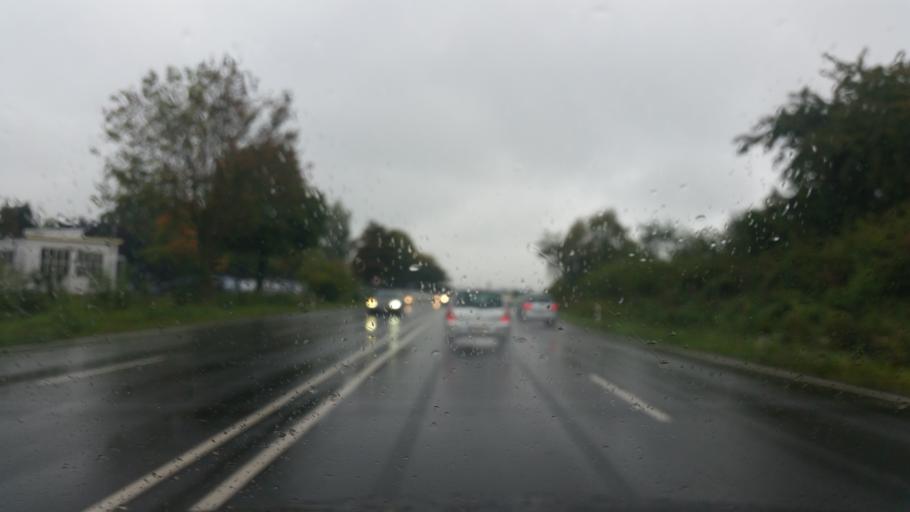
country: DE
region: Lower Saxony
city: Ronnenberg
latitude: 52.3275
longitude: 9.6835
